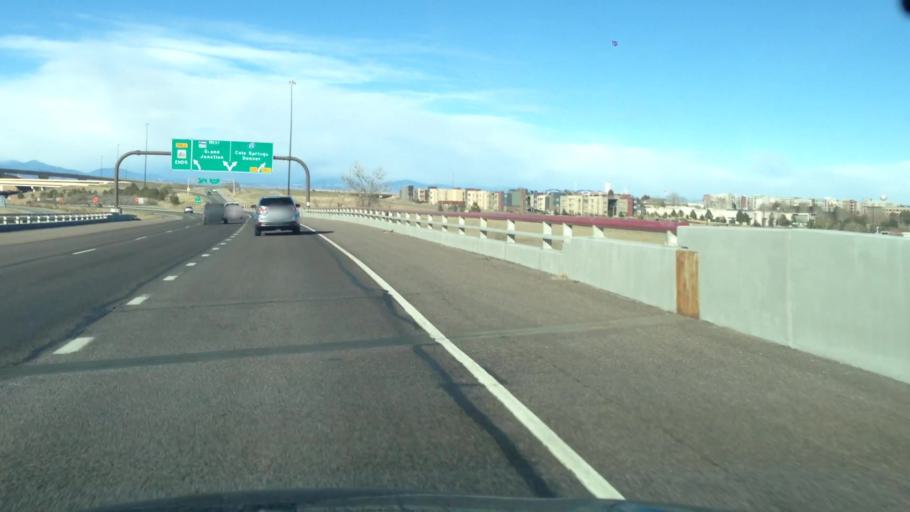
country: US
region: Colorado
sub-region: Douglas County
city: Meridian
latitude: 39.5540
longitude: -104.8610
